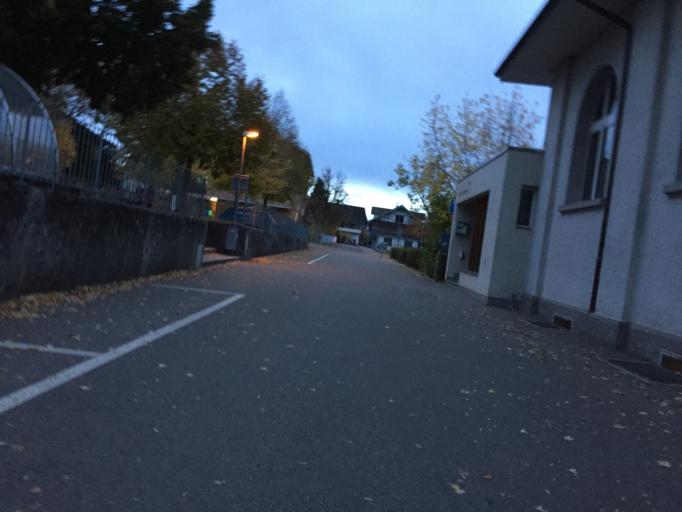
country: CH
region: Bern
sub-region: Bern-Mittelland District
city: Munsingen
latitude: 46.8774
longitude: 7.5637
